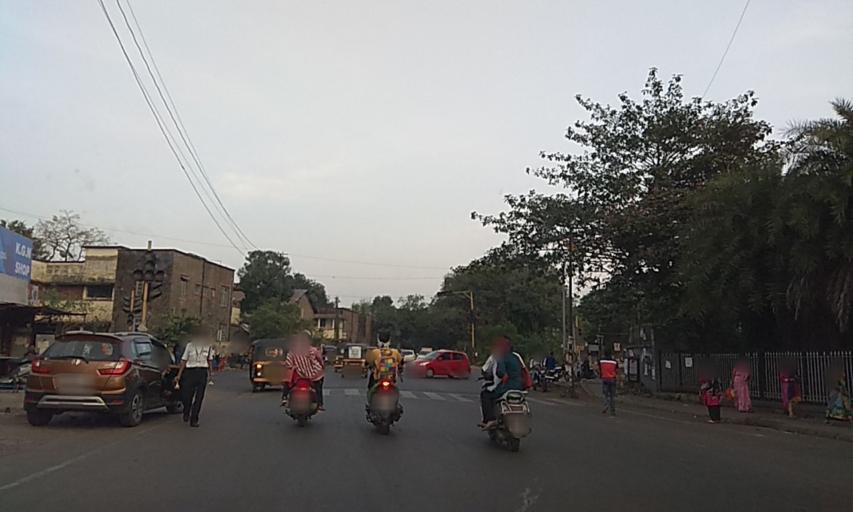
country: IN
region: Maharashtra
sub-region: Pune Division
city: Khadki
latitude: 18.5641
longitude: 73.8846
